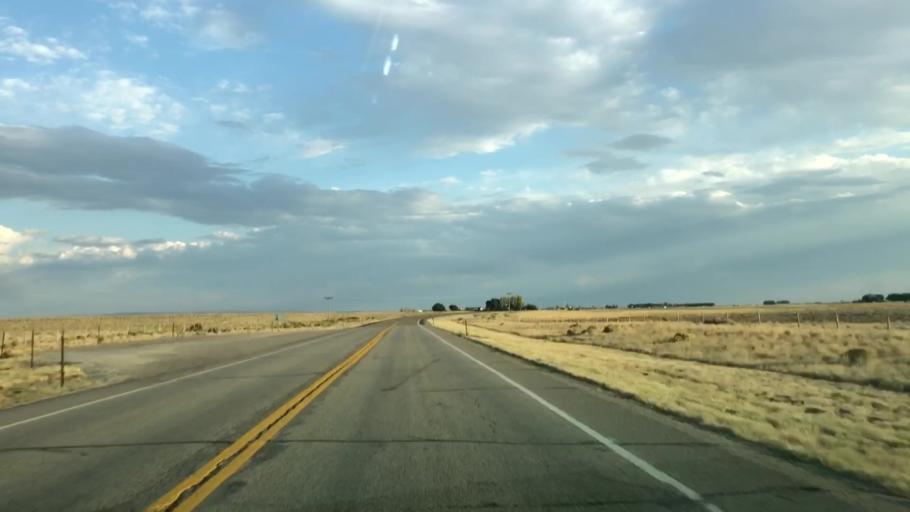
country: US
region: Wyoming
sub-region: Sweetwater County
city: North Rock Springs
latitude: 42.0881
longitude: -109.4398
